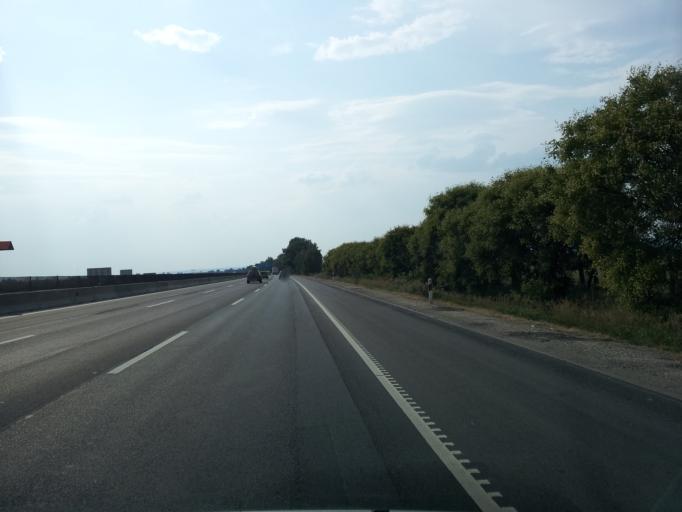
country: HU
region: Pest
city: Dunaharaszti
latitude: 47.3754
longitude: 19.0808
